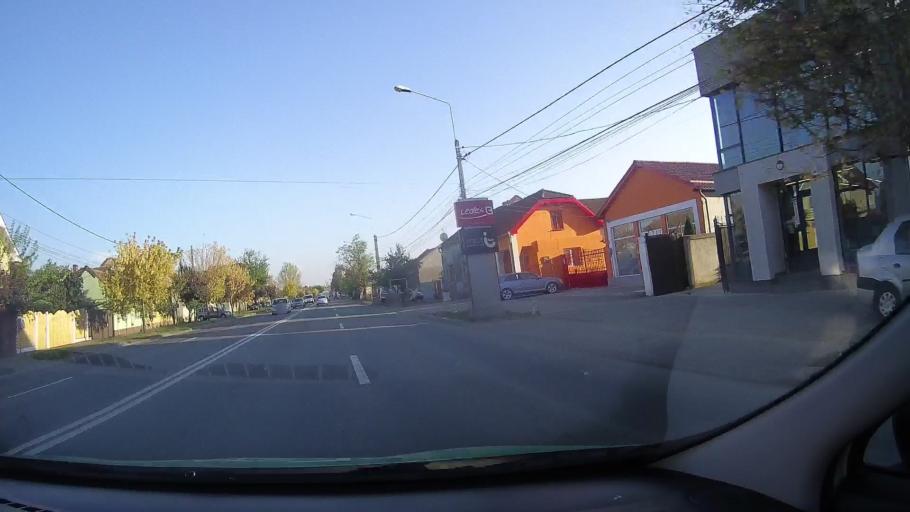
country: RO
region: Bihor
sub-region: Comuna Biharea
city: Oradea
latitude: 47.0945
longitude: 21.9035
